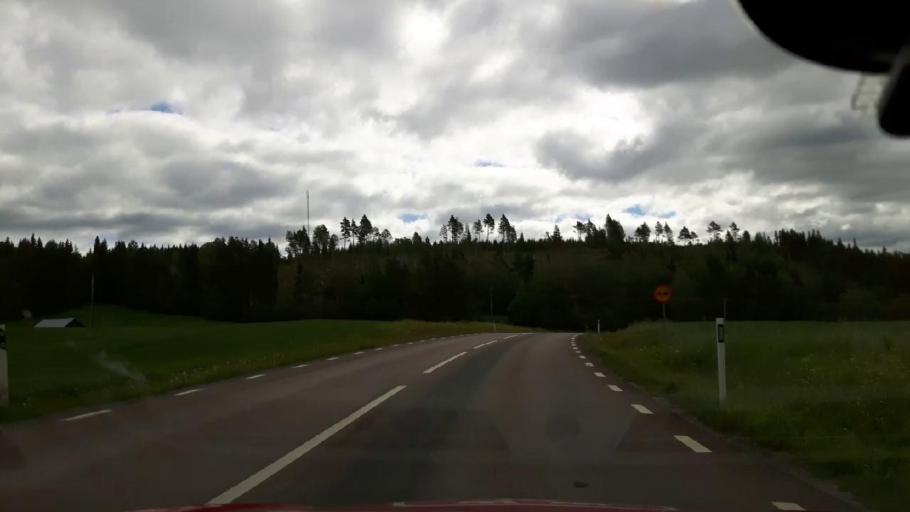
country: SE
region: Jaemtland
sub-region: OEstersunds Kommun
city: Brunflo
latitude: 63.0180
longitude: 14.9444
